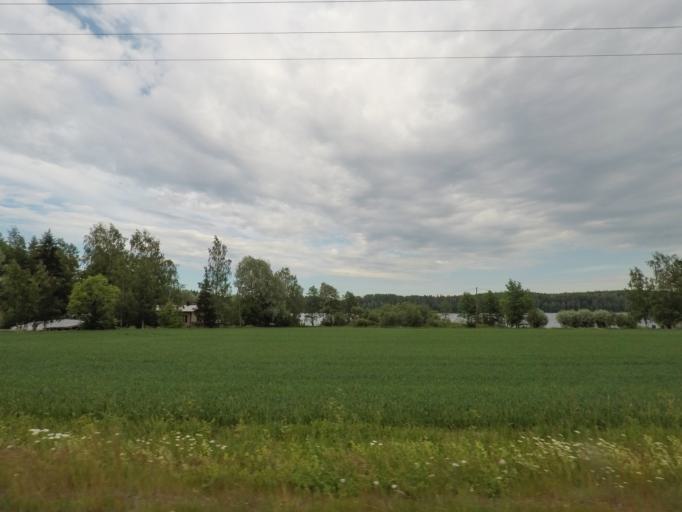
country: FI
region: Uusimaa
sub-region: Porvoo
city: Pukkila
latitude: 60.7594
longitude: 25.4396
